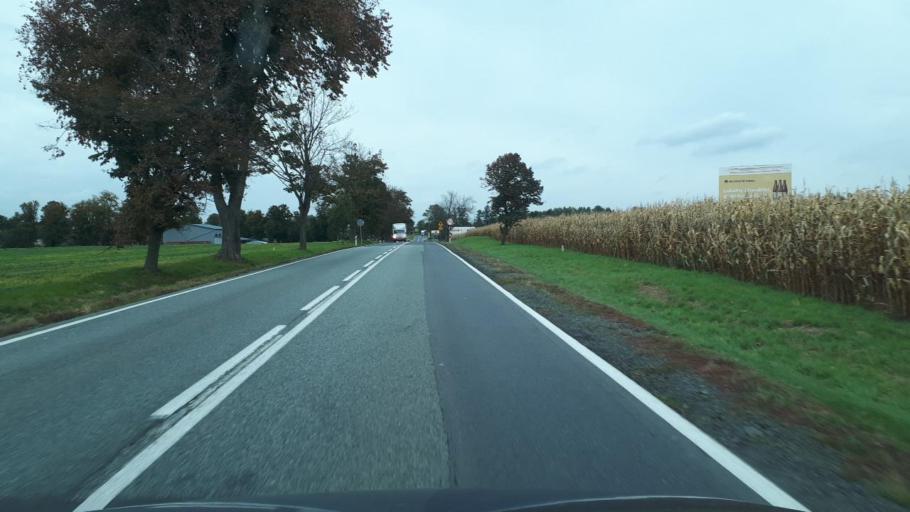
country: PL
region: Opole Voivodeship
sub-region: Powiat kluczborski
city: Byczyna
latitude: 51.0787
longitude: 18.2003
